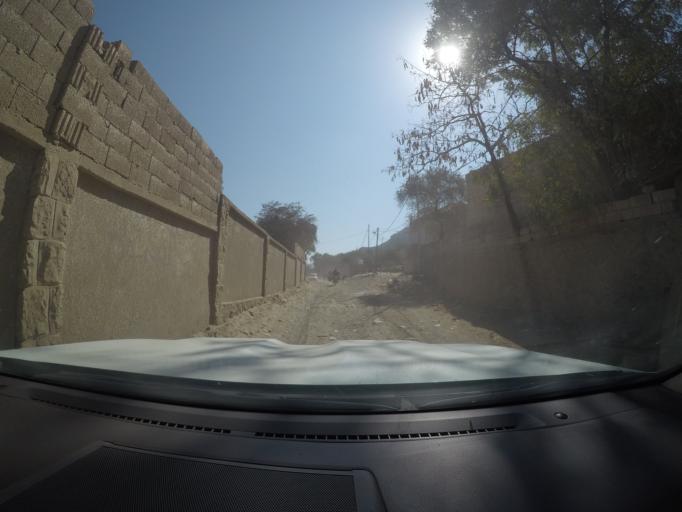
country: YE
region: Ad Dali'
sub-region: Ad Dhale'e
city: Dhalie
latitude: 13.7026
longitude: 44.7364
